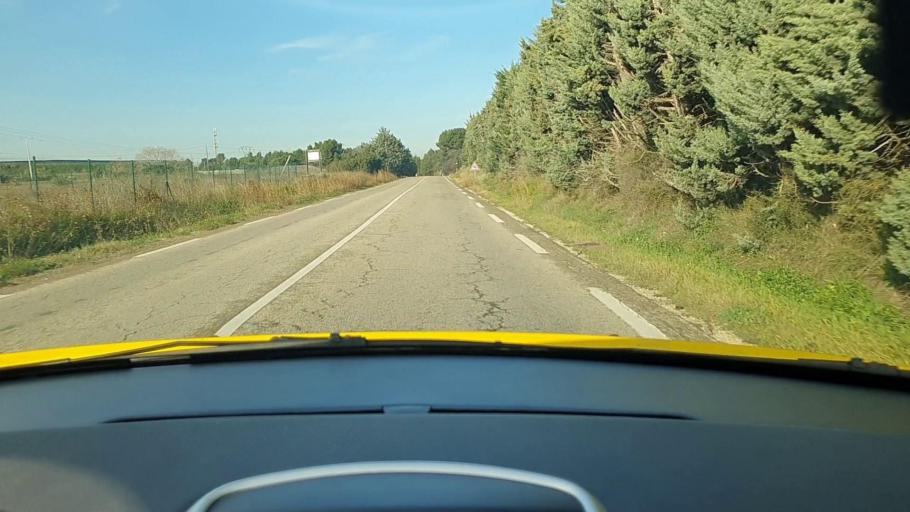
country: FR
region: Languedoc-Roussillon
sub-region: Departement du Gard
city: Comps
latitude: 43.8228
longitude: 4.5984
